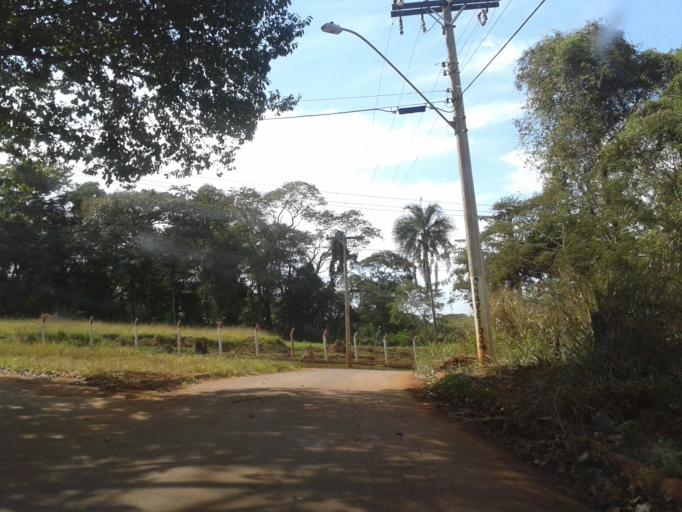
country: BR
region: Goias
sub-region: Goiania
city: Goiania
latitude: -16.6445
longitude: -49.3480
